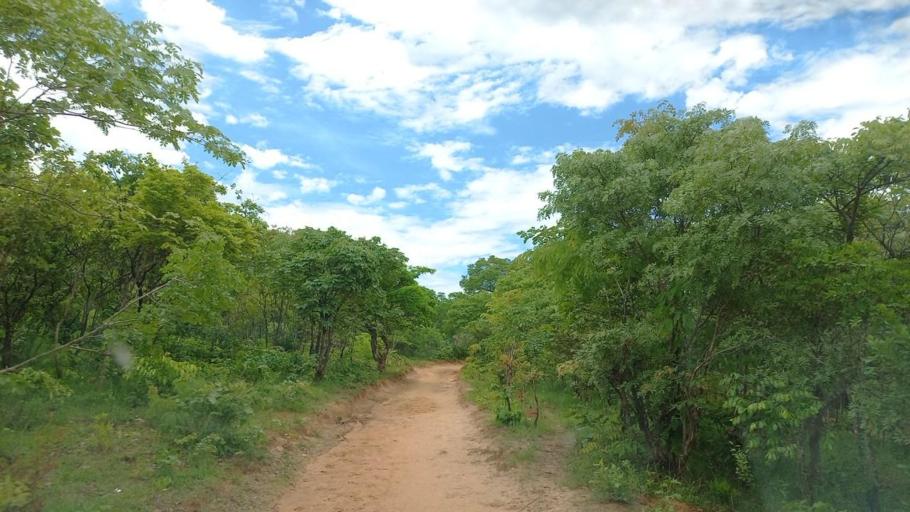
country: ZM
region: North-Western
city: Kabompo
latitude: -13.6079
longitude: 24.2497
